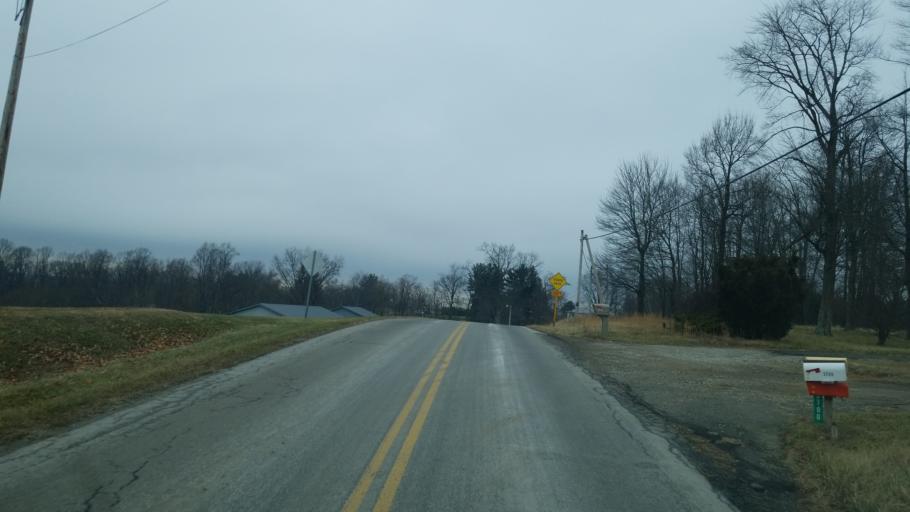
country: US
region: Ohio
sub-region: Holmes County
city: Millersburg
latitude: 40.5137
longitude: -81.8963
